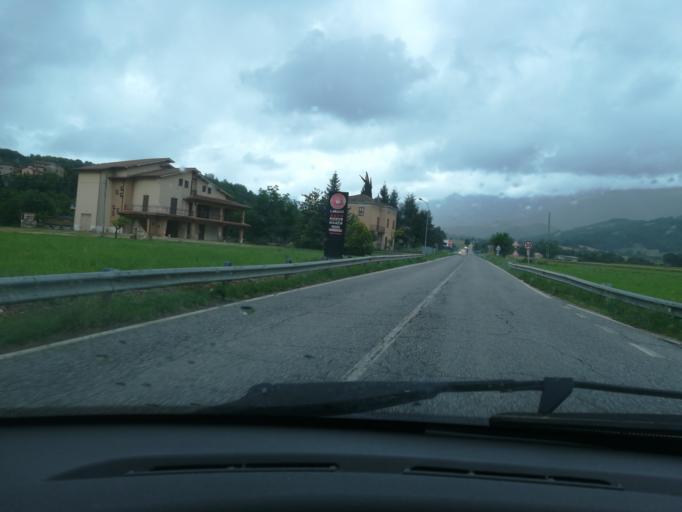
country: IT
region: The Marches
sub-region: Provincia di Macerata
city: Cessapalombo
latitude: 43.0762
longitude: 13.2797
